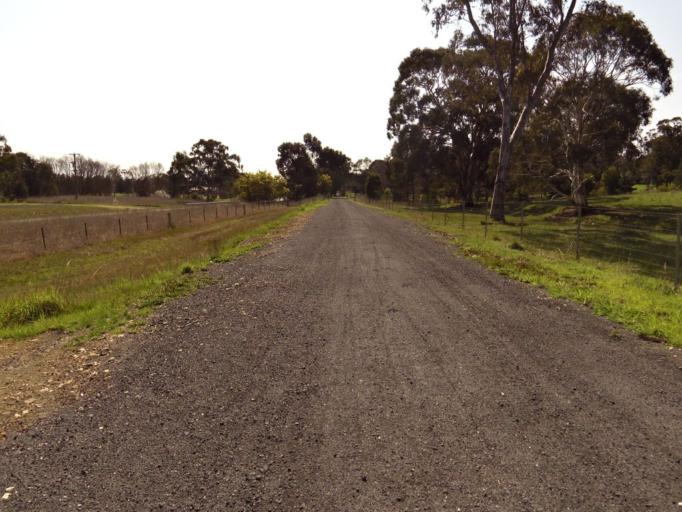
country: AU
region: Victoria
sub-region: Murrindindi
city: Alexandra
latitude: -37.1303
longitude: 145.5948
